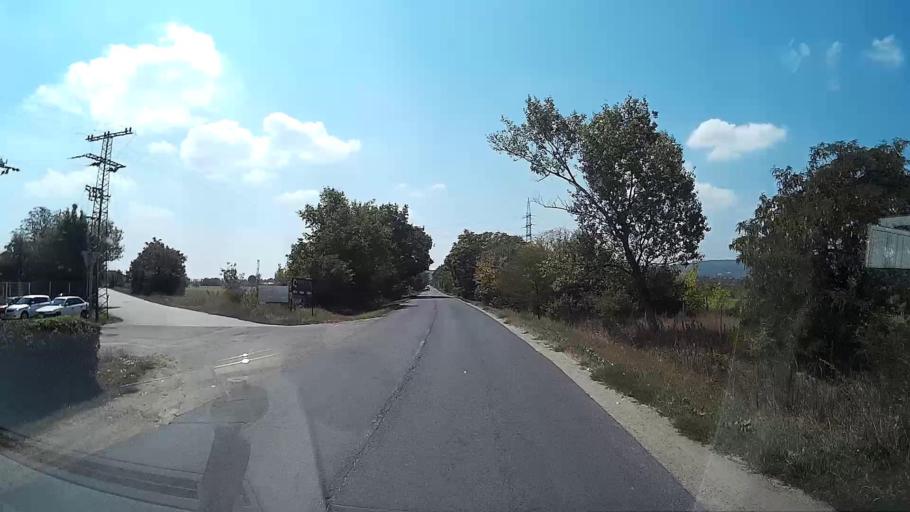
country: HU
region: Pest
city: Budakalasz
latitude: 47.6387
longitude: 19.0647
